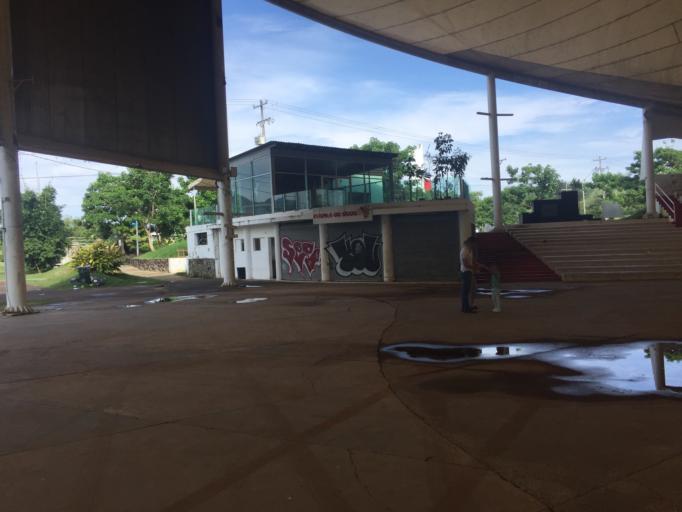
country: MX
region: Nayarit
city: Tepic
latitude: 21.4897
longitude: -104.8599
